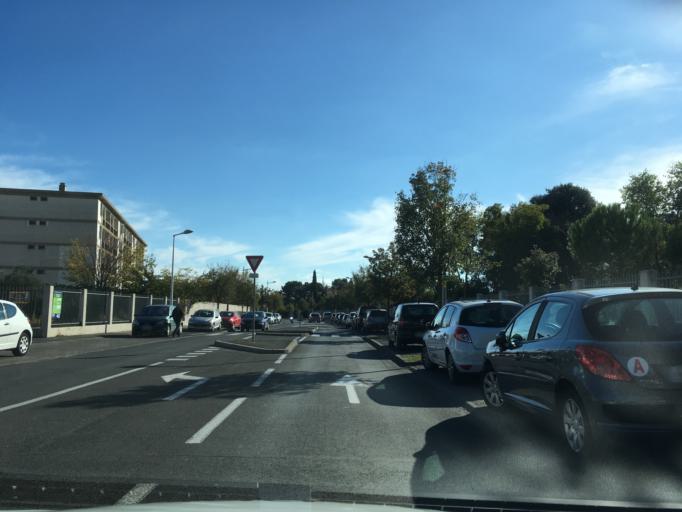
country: FR
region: Languedoc-Roussillon
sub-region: Departement de l'Herault
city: Montpellier
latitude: 43.6103
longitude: 3.8465
